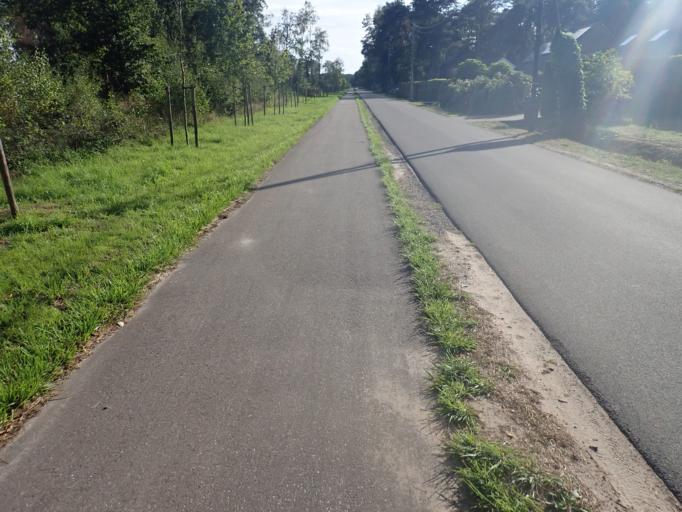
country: BE
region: Flanders
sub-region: Provincie Antwerpen
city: Zoersel
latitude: 51.2693
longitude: 4.6824
